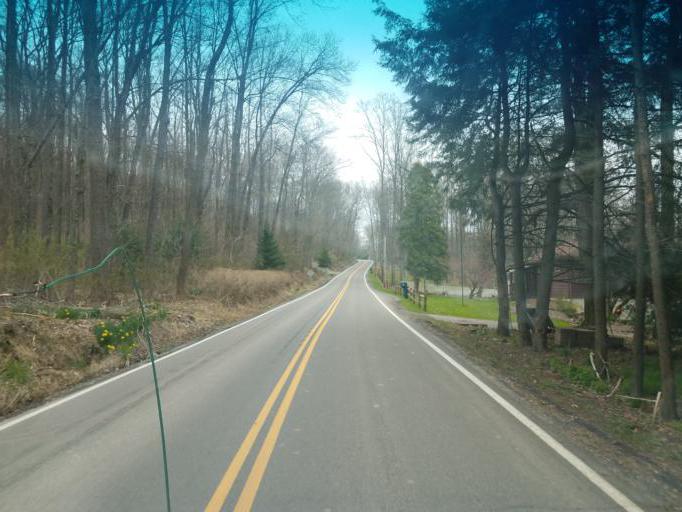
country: US
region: Ohio
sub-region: Stark County
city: Beach City
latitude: 40.6055
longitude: -81.6715
